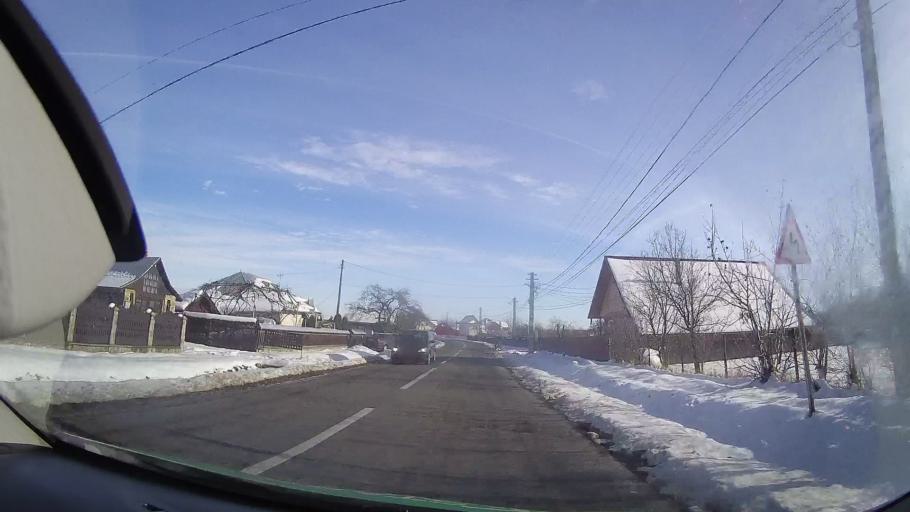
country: RO
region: Neamt
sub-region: Comuna Agapia
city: Agapia
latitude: 47.1725
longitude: 26.2912
